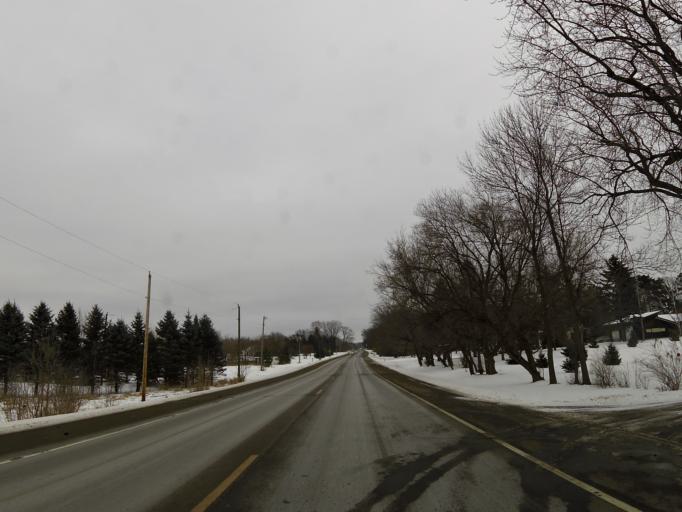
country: US
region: Minnesota
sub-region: Washington County
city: Lake Elmo
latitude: 45.0072
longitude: -92.8474
